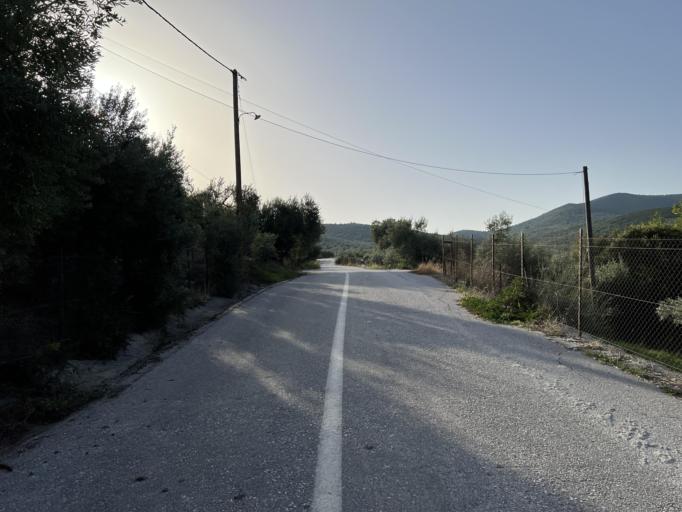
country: GR
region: Thessaly
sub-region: Nomos Magnisias
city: Sourpi
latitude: 39.1644
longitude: 22.8943
